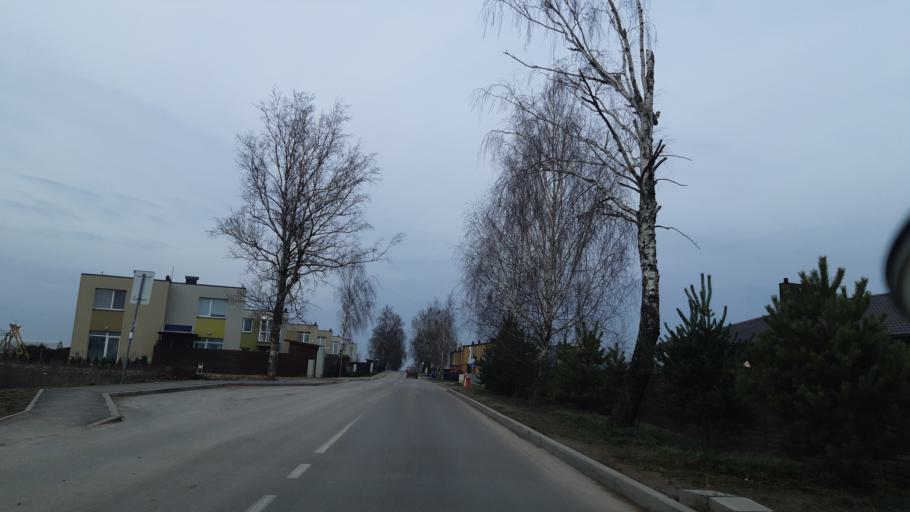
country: LT
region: Kauno apskritis
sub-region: Kauno rajonas
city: Akademija (Kaunas)
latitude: 54.9476
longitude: 23.8286
